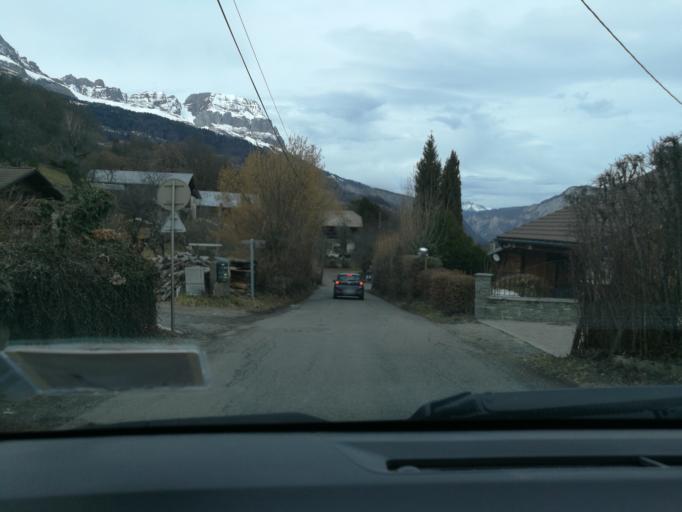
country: FR
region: Rhone-Alpes
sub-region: Departement de la Haute-Savoie
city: Cordon
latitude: 45.9230
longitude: 6.6277
